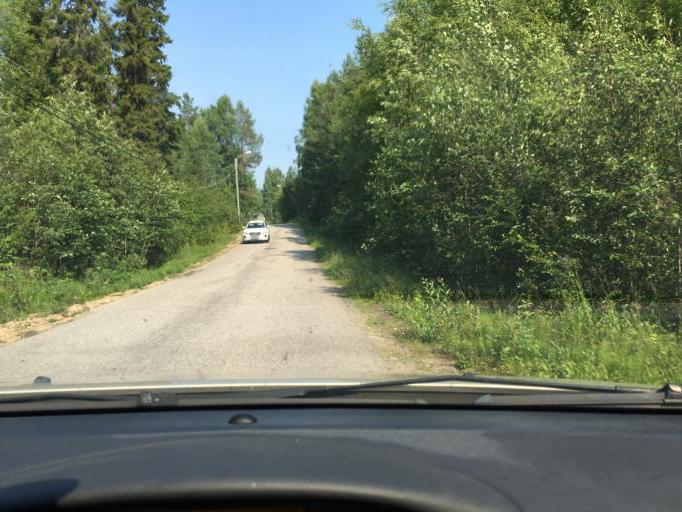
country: SE
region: Norrbotten
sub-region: Kalix Kommun
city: Kalix
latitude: 65.7750
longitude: 23.1925
